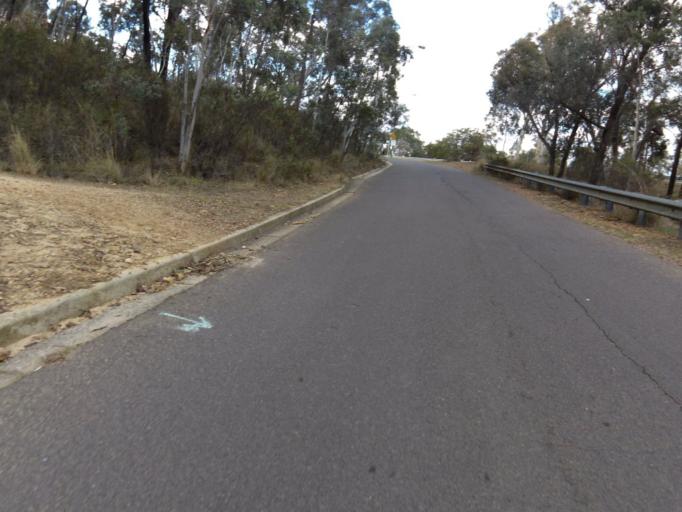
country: AU
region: Australian Capital Territory
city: Acton
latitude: -35.2654
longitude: 149.1103
